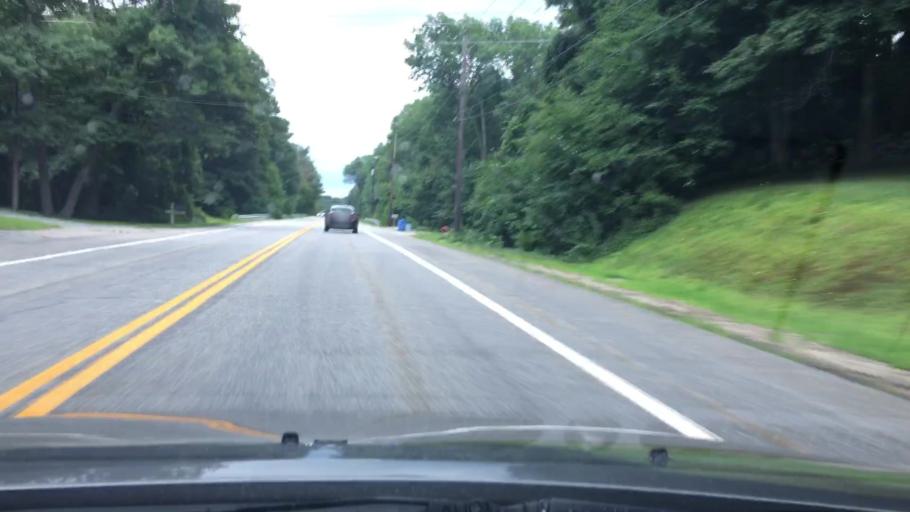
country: US
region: Rhode Island
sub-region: Providence County
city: Cumberland
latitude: 42.0088
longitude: -71.4281
